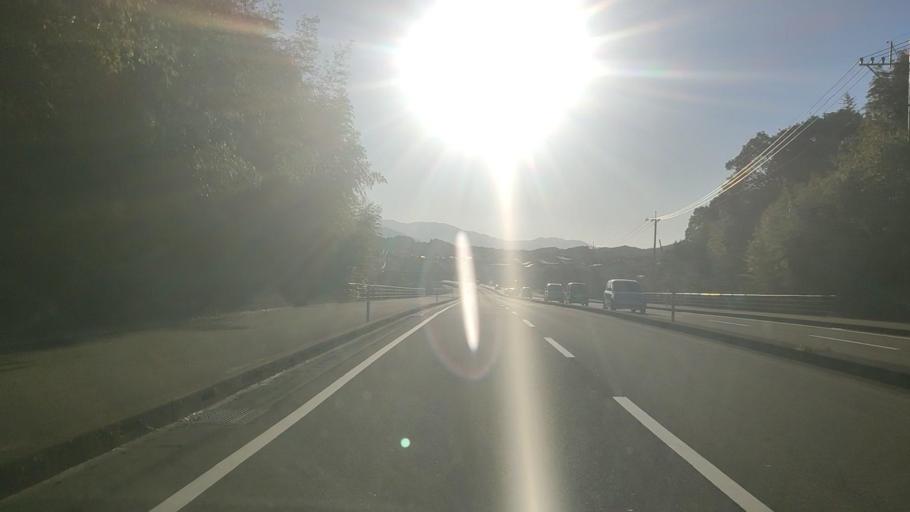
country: JP
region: Miyazaki
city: Miyazaki-shi
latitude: 31.8828
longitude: 131.3967
